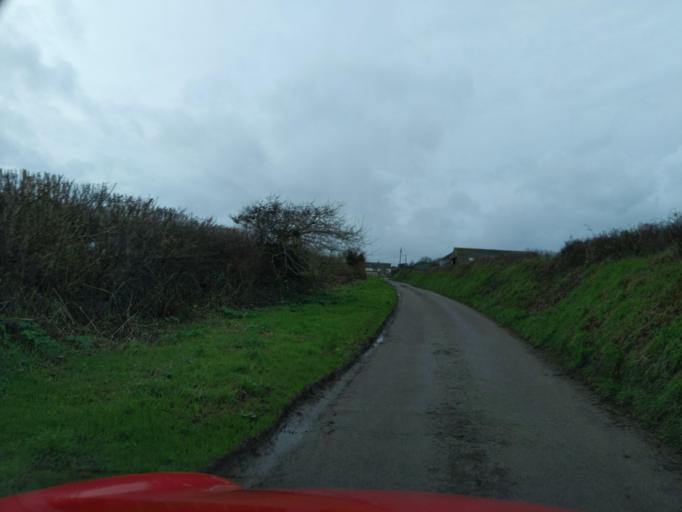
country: GB
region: England
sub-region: Cornwall
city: Duloe
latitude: 50.3484
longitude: -4.5403
